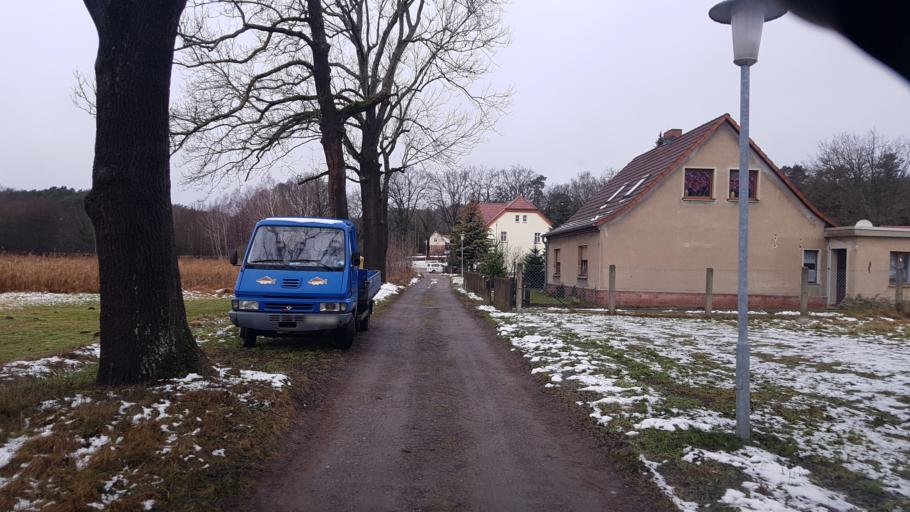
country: DE
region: Brandenburg
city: Jamlitz
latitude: 51.9921
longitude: 14.3492
